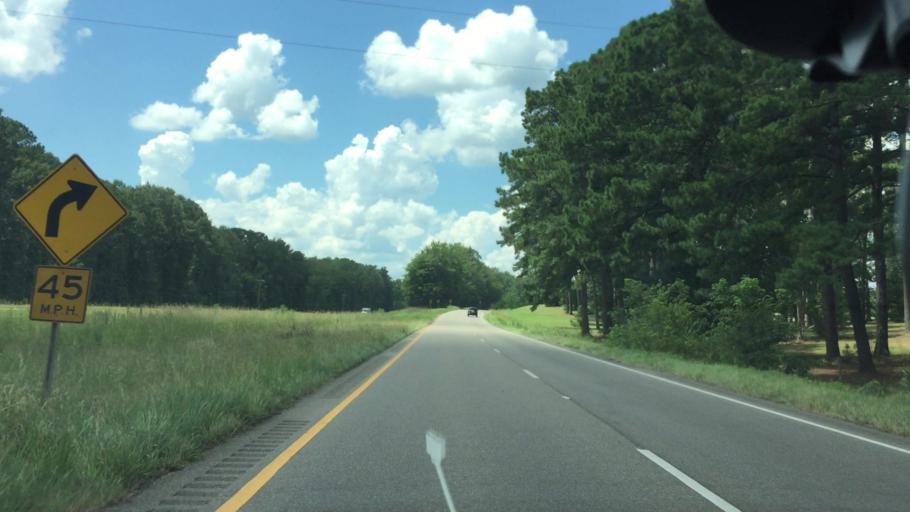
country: US
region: Alabama
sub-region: Montgomery County
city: Pike Road
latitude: 32.1480
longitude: -86.1055
